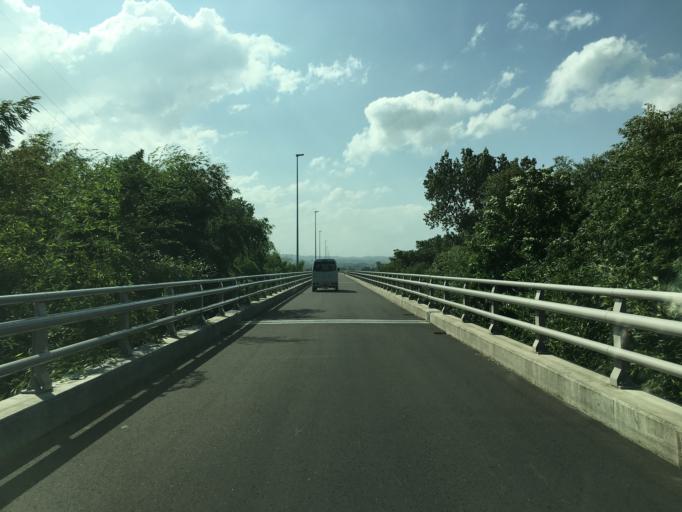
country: JP
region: Miyagi
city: Kakuda
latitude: 37.9585
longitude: 140.7942
